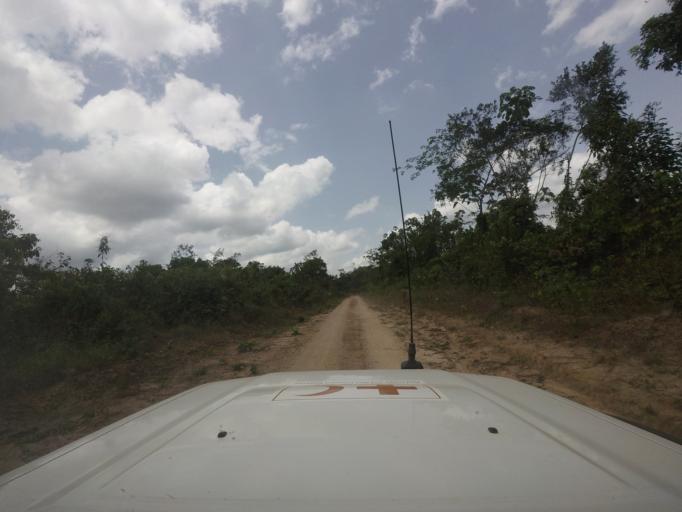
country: GN
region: Nzerekore
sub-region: Yomou
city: Yomou
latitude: 7.2617
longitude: -9.1892
